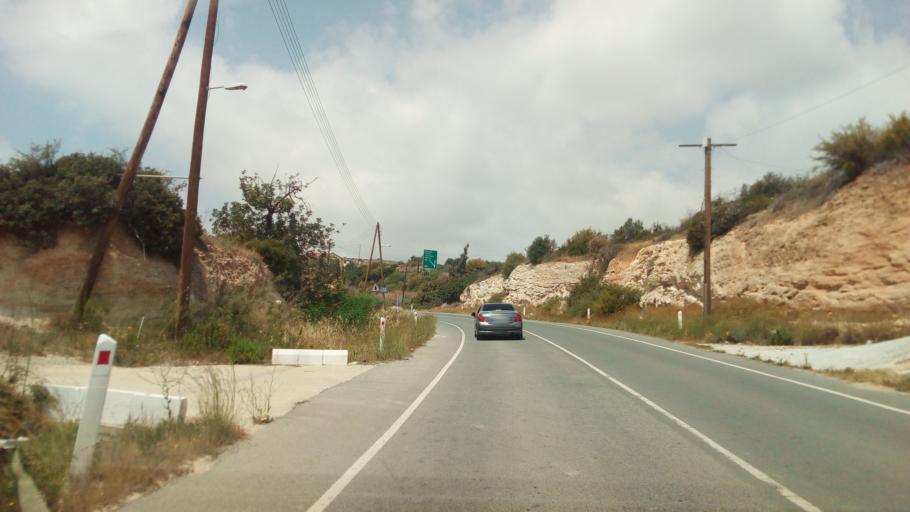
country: CY
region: Limassol
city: Pissouri
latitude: 34.6832
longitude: 32.7056
